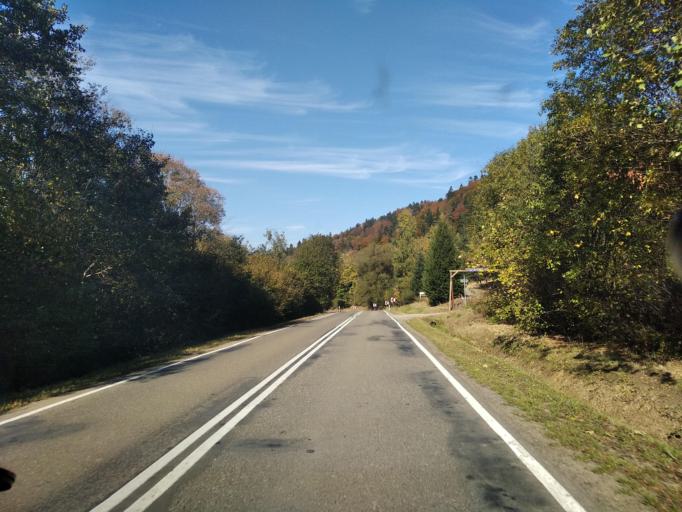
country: PL
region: Subcarpathian Voivodeship
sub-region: Powiat leski
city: Baligrod
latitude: 49.3089
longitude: 22.2772
